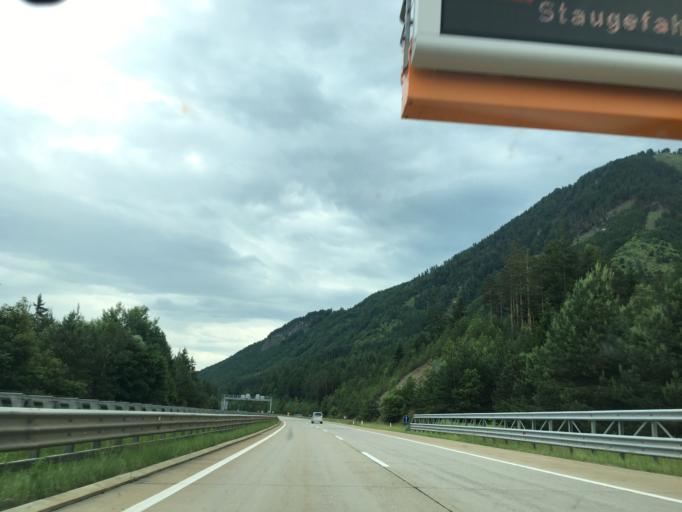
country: AT
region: Carinthia
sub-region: Politischer Bezirk Villach Land
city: Fresach
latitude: 46.6536
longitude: 13.7405
